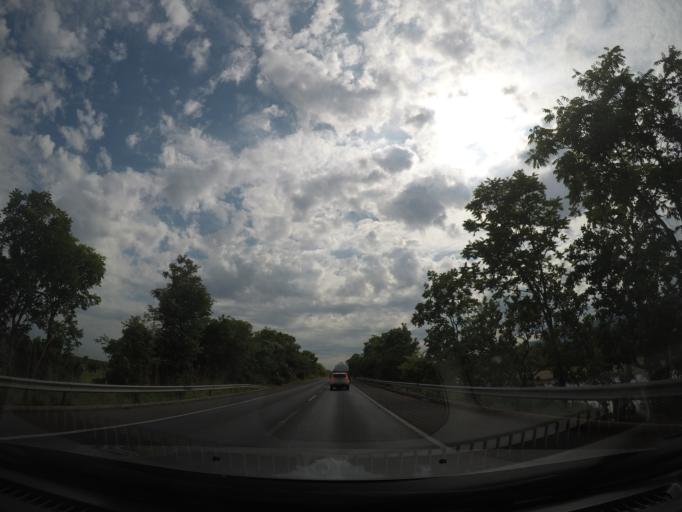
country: BR
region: Goias
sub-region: Formosa
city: Formosa
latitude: -14.9164
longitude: -46.9529
